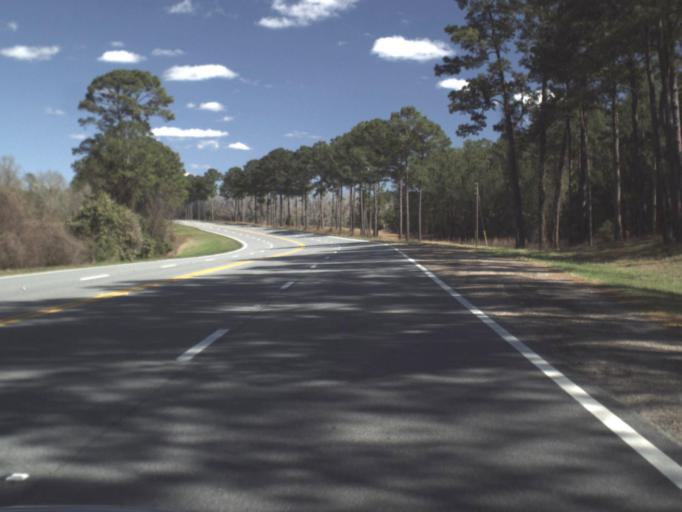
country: US
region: Florida
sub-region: Gadsden County
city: Chattahoochee
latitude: 30.7006
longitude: -84.8110
